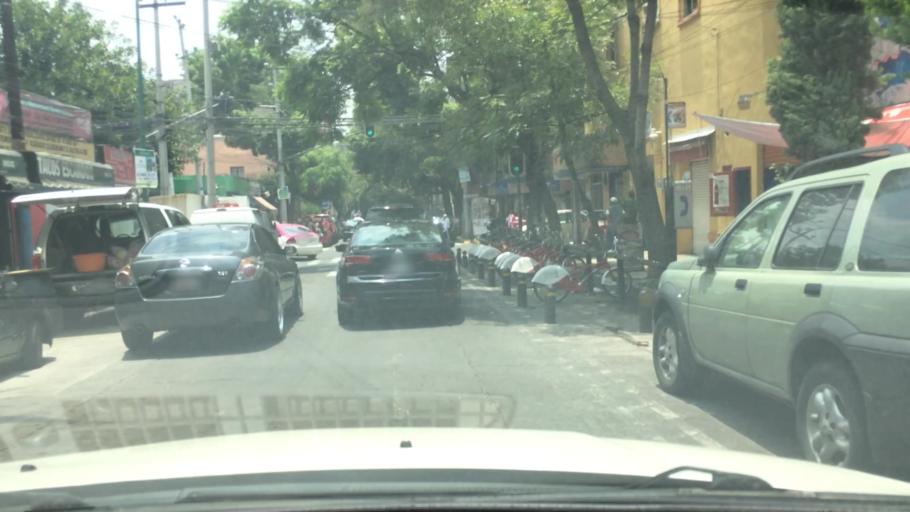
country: MX
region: Mexico City
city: Benito Juarez
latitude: 19.4015
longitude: -99.1765
